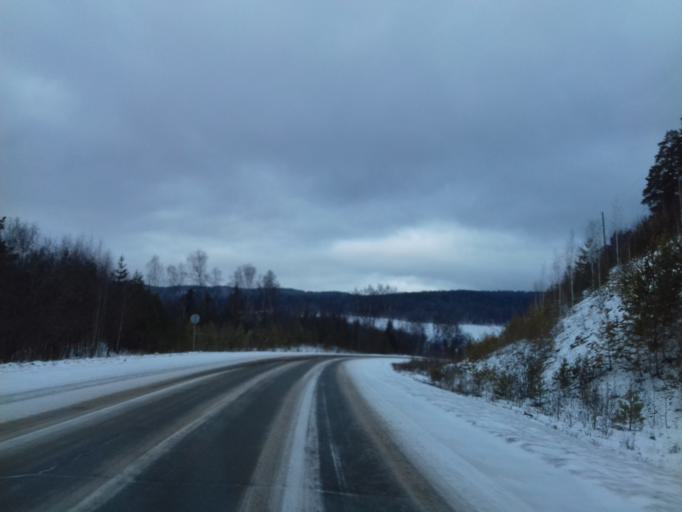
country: RU
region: Bashkortostan
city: Starosubkhangulovo
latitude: 53.2297
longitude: 57.4695
